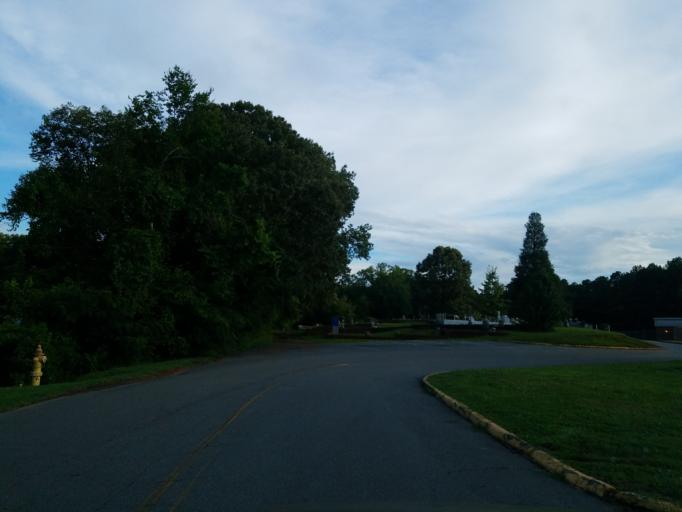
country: US
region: Georgia
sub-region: Bartow County
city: Emerson
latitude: 34.1243
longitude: -84.7573
